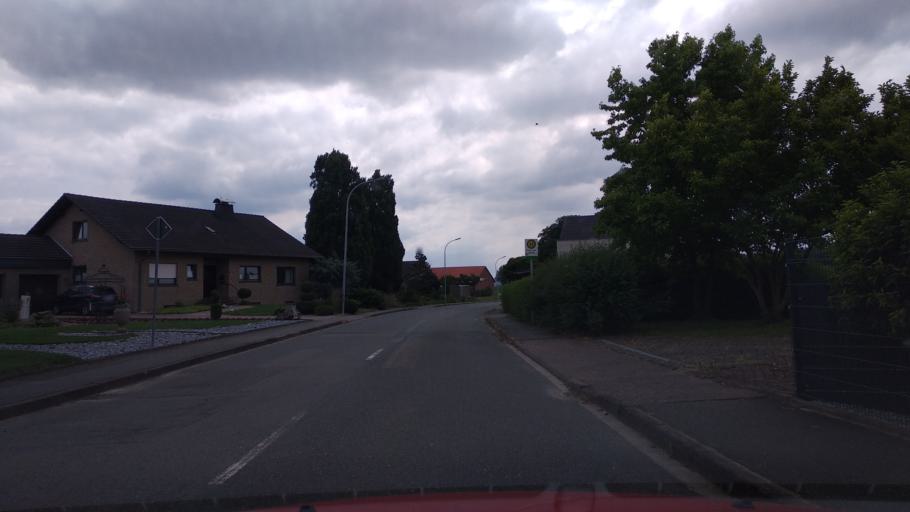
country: DE
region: North Rhine-Westphalia
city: Borgentreich
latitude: 51.5389
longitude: 9.2054
